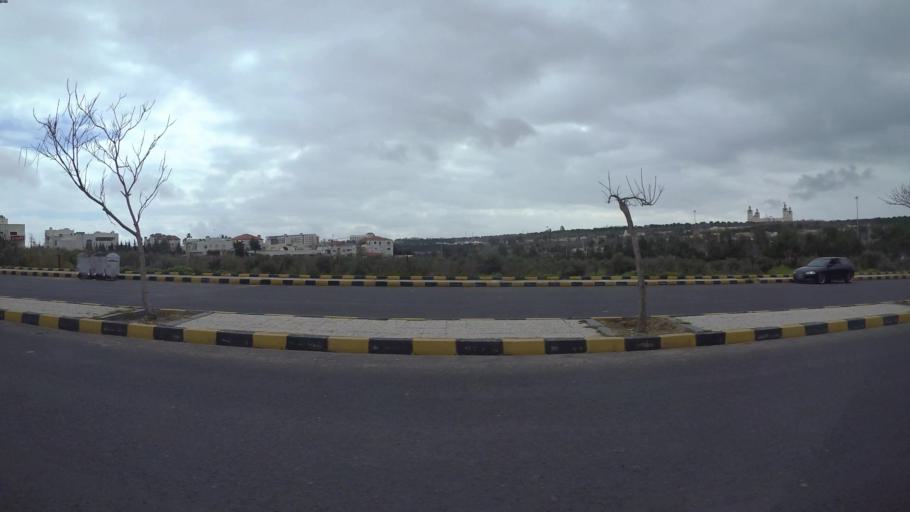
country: JO
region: Amman
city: Wadi as Sir
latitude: 31.9901
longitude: 35.8319
